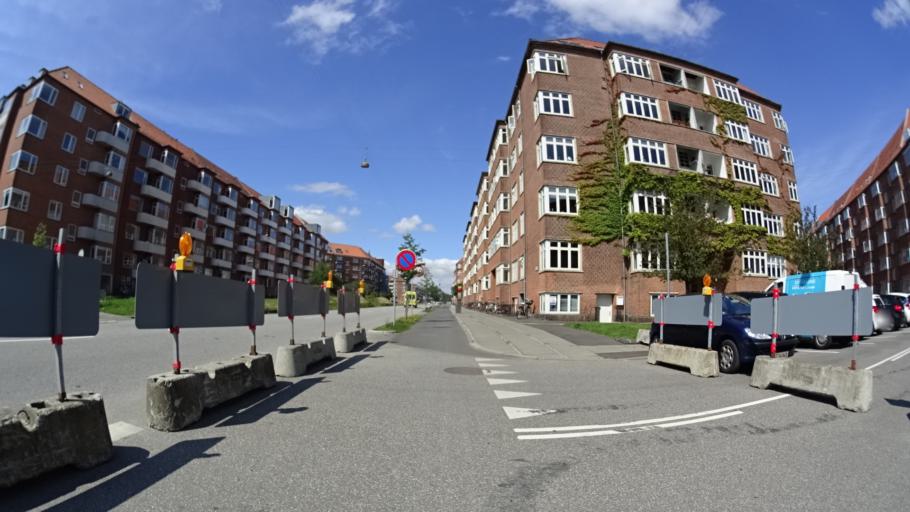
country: DK
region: Central Jutland
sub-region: Arhus Kommune
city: Arhus
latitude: 56.1420
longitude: 10.1927
